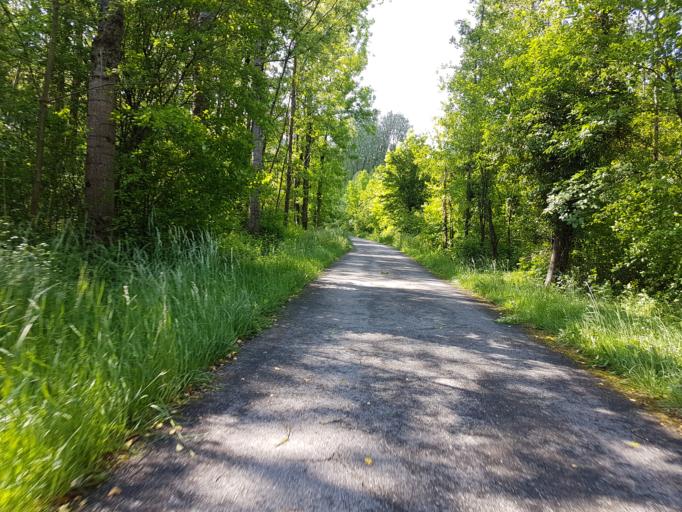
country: FR
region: Rhone-Alpes
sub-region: Departement de l'Ain
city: Culoz
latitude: 45.8120
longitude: 5.7912
